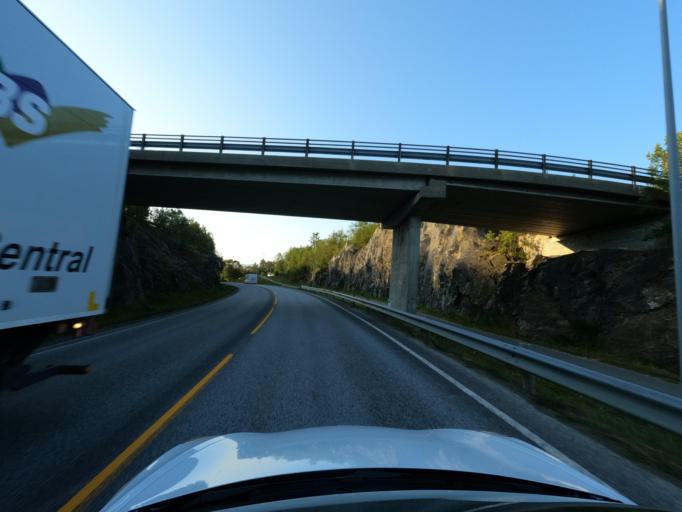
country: NO
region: Troms
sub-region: Harstad
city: Harstad
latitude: 68.7522
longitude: 16.5673
